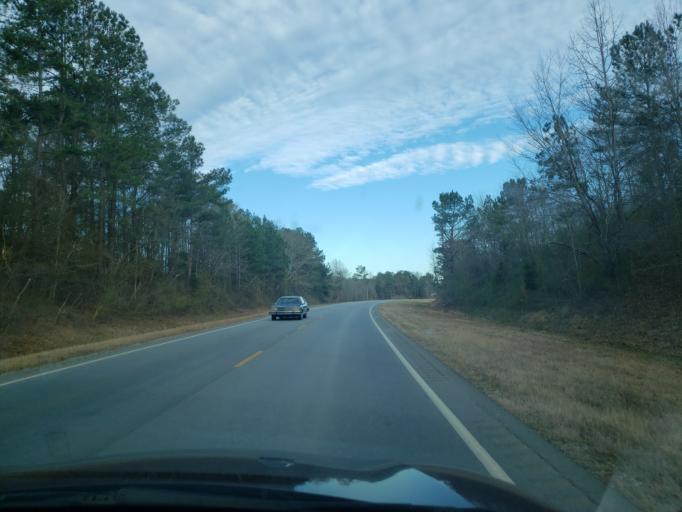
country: US
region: Alabama
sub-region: Randolph County
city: Wedowee
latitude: 33.4115
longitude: -85.5438
